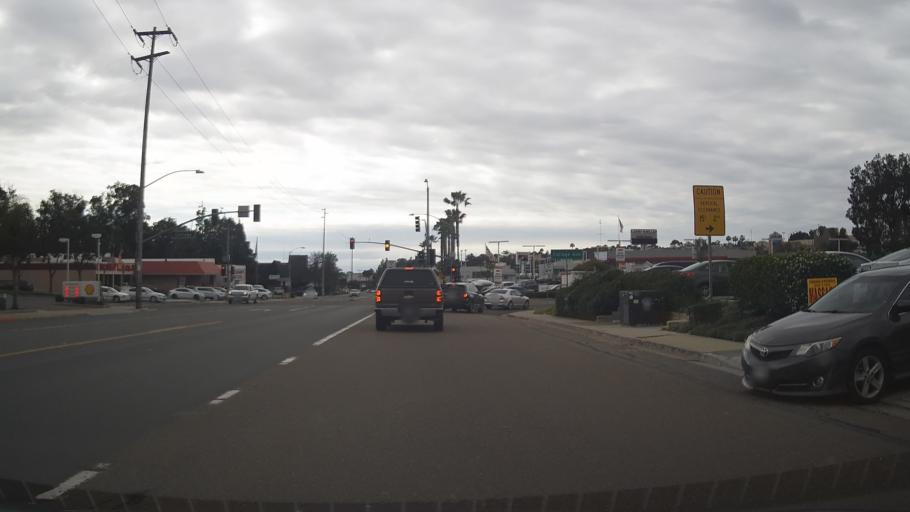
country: US
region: California
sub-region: San Diego County
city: Lemon Grove
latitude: 32.7415
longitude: -117.0492
